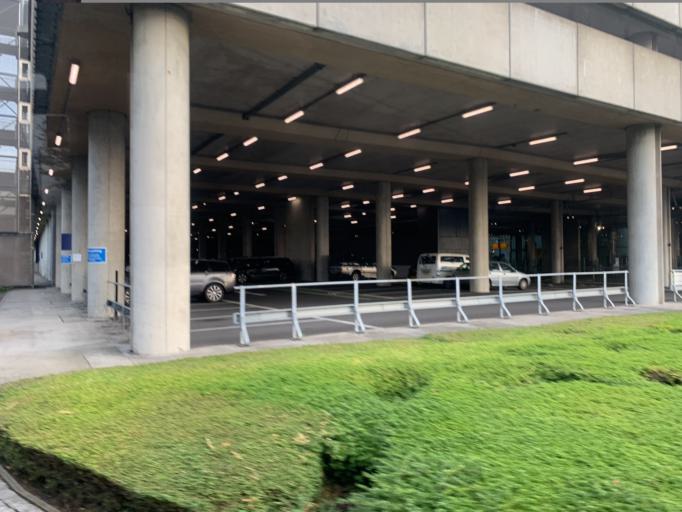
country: GB
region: England
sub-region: Buckinghamshire
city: Iver
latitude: 51.4701
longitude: -0.4902
